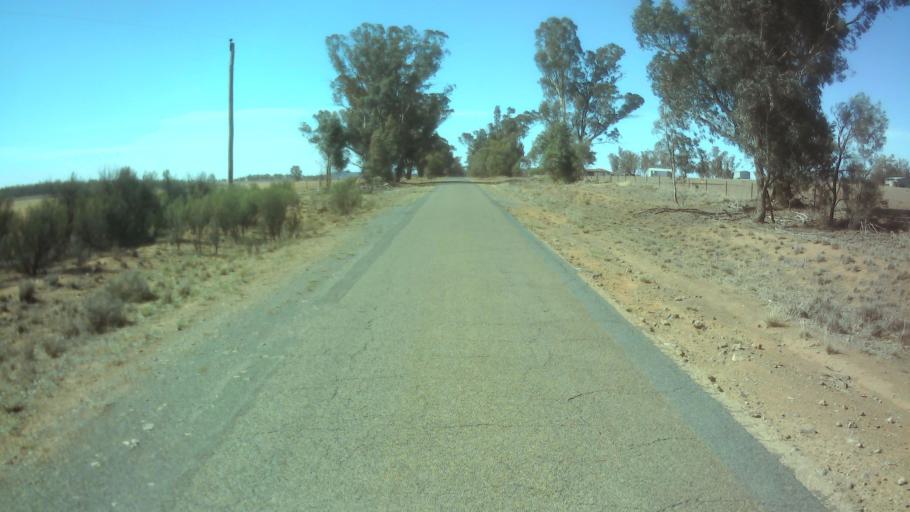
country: AU
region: New South Wales
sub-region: Forbes
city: Forbes
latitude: -33.7281
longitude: 147.7437
